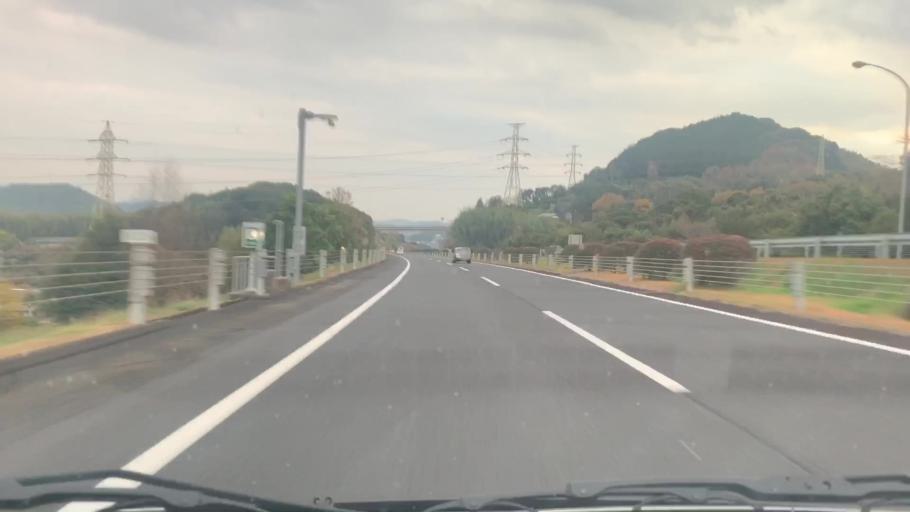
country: JP
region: Nagasaki
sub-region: Isahaya-shi
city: Isahaya
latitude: 32.8598
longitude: 130.0034
